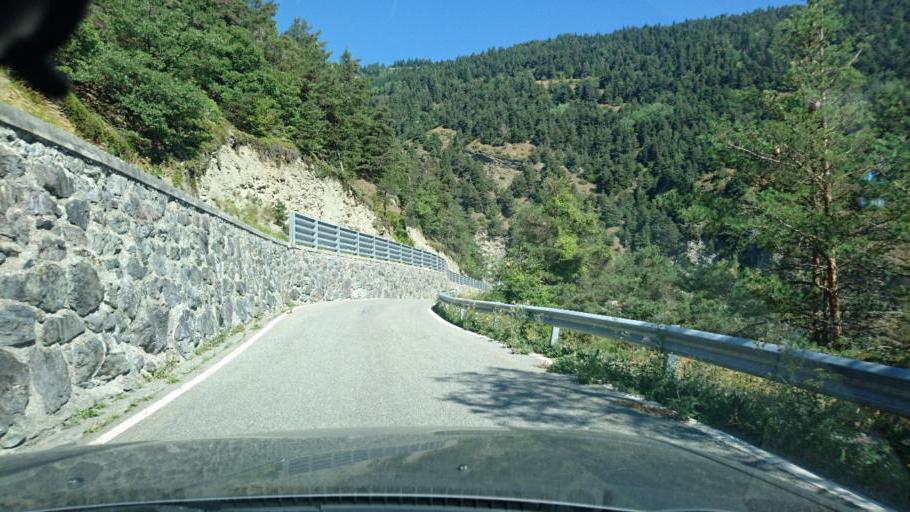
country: IT
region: Aosta Valley
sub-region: Valle d'Aosta
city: Montan-Angelin-Arensod
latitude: 45.7491
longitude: 7.2763
